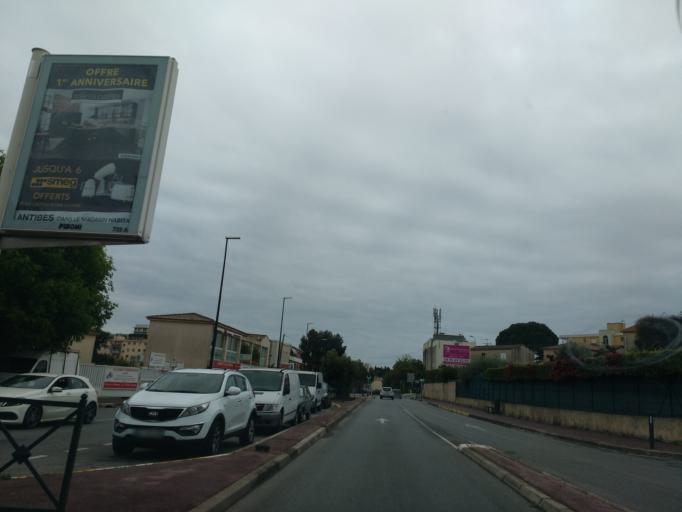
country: FR
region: Provence-Alpes-Cote d'Azur
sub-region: Departement des Alpes-Maritimes
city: Le Cannet
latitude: 43.5686
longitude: 7.0022
